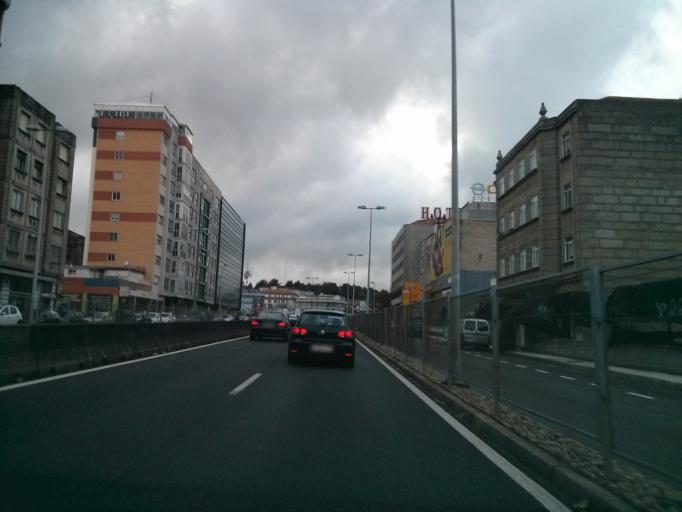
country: ES
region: Galicia
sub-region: Provincia de Pontevedra
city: Vigo
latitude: 42.2269
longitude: -8.7161
